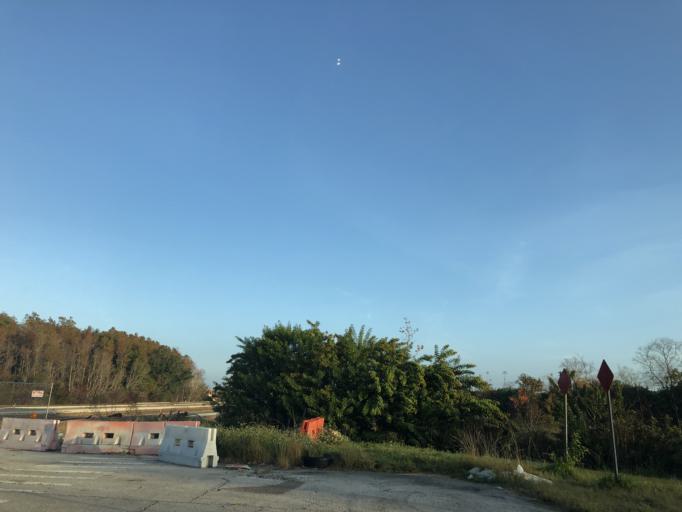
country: US
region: Florida
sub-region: Osceola County
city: Kissimmee
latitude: 28.3309
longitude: -81.4242
